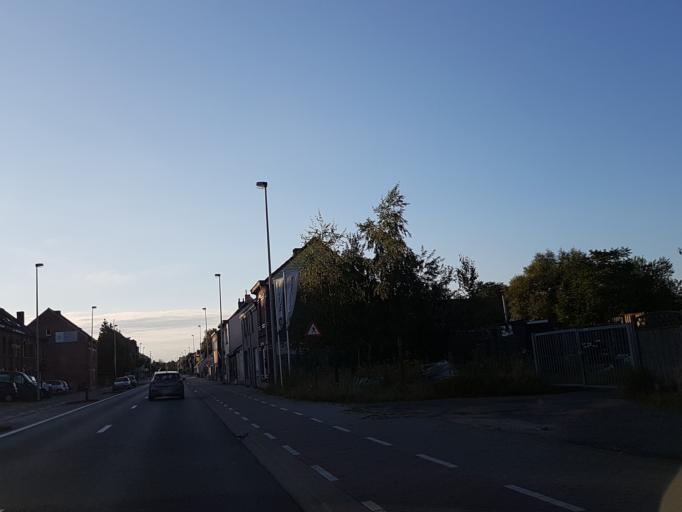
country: BE
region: Flanders
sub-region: Provincie Oost-Vlaanderen
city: Lebbeke
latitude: 51.0100
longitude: 4.1179
